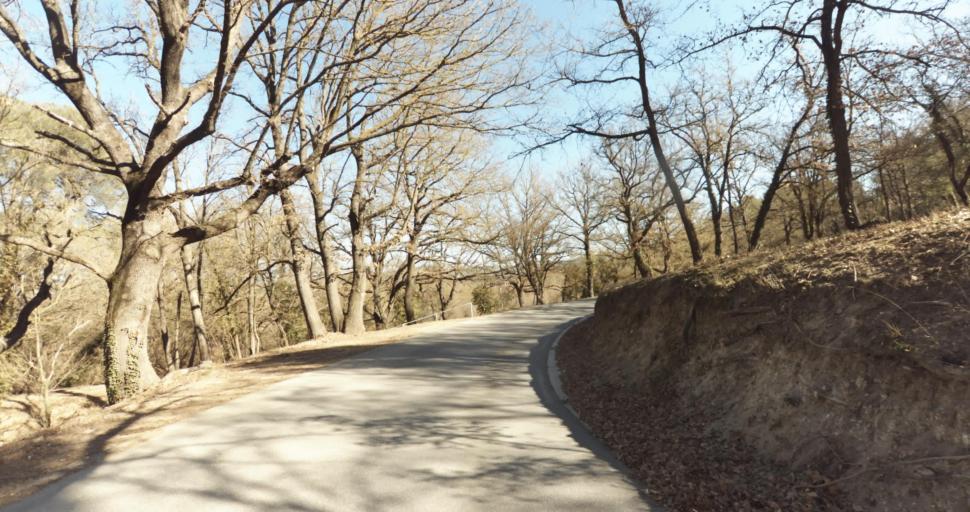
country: FR
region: Provence-Alpes-Cote d'Azur
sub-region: Departement des Bouches-du-Rhone
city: Peypin
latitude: 43.3945
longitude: 5.5663
